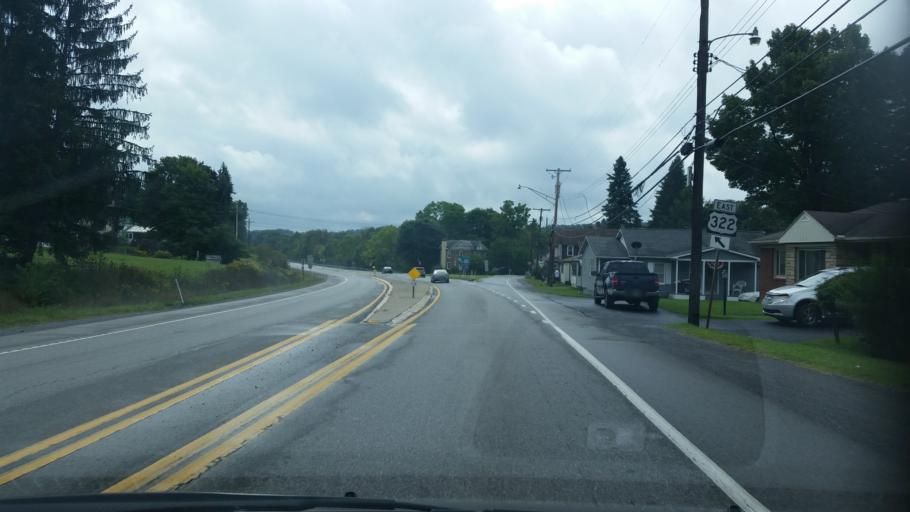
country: US
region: Pennsylvania
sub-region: Clearfield County
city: Troy
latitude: 40.9320
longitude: -78.2806
